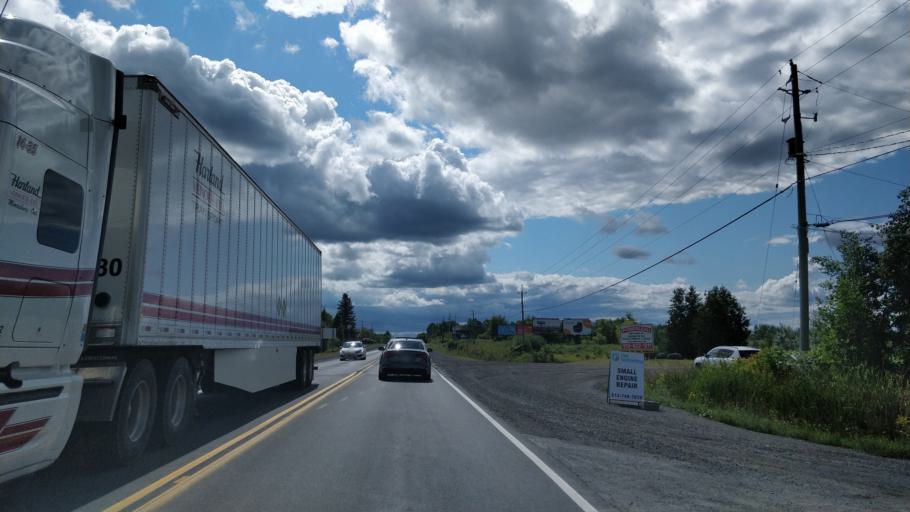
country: CA
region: Ontario
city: Ottawa
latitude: 45.2937
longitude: -75.5782
